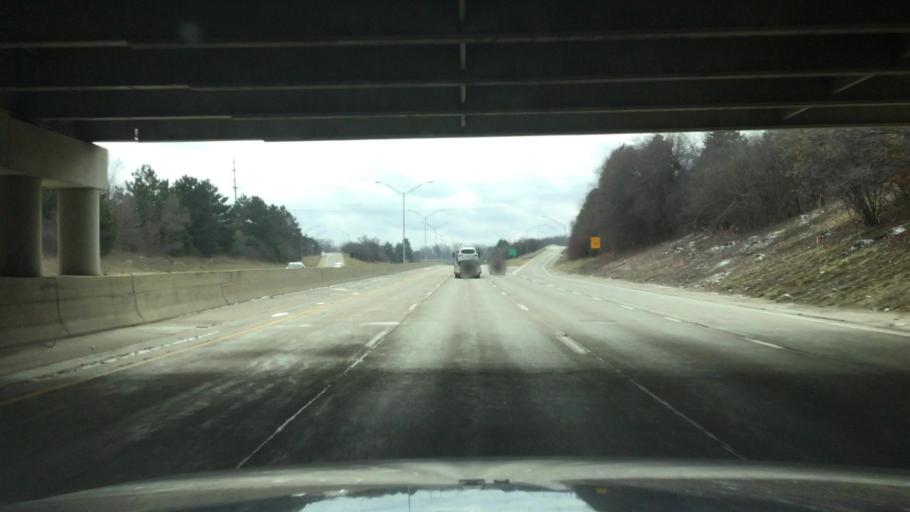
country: US
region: Michigan
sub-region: Genesee County
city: Beecher
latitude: 43.0758
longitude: -83.6838
